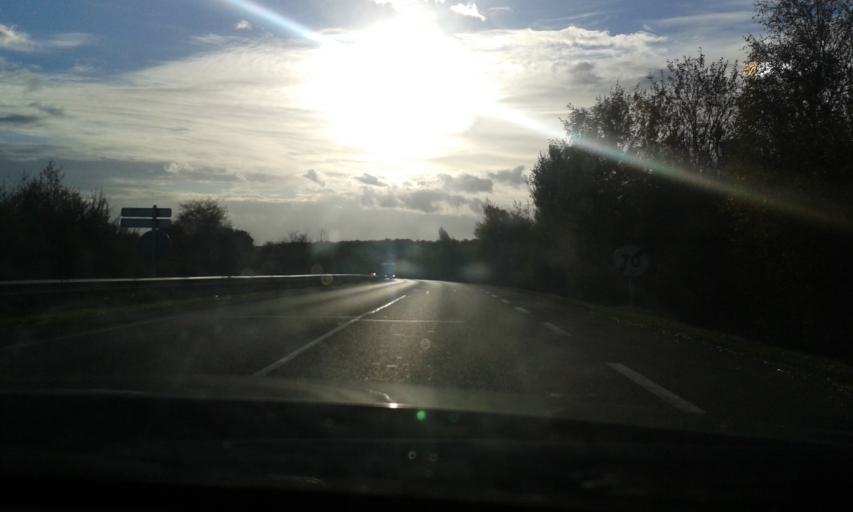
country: FR
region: Centre
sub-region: Departement d'Eure-et-Loir
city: Leves
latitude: 48.4852
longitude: 1.4664
